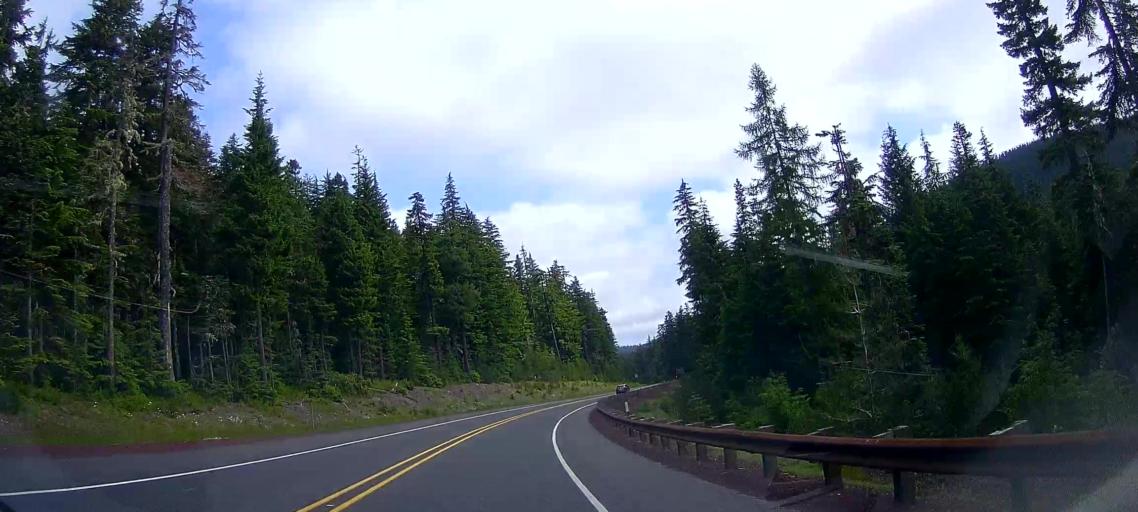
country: US
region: Oregon
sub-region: Clackamas County
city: Mount Hood Village
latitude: 45.2207
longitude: -121.6987
